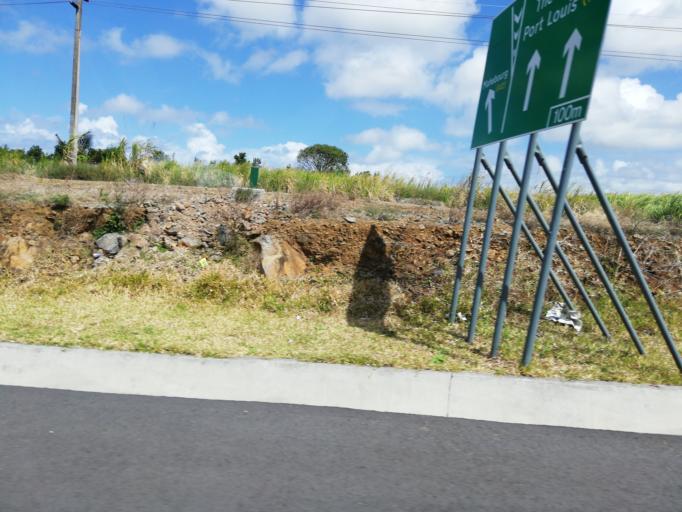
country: MU
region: Grand Port
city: Plaine Magnien
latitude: -20.4349
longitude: 57.6483
